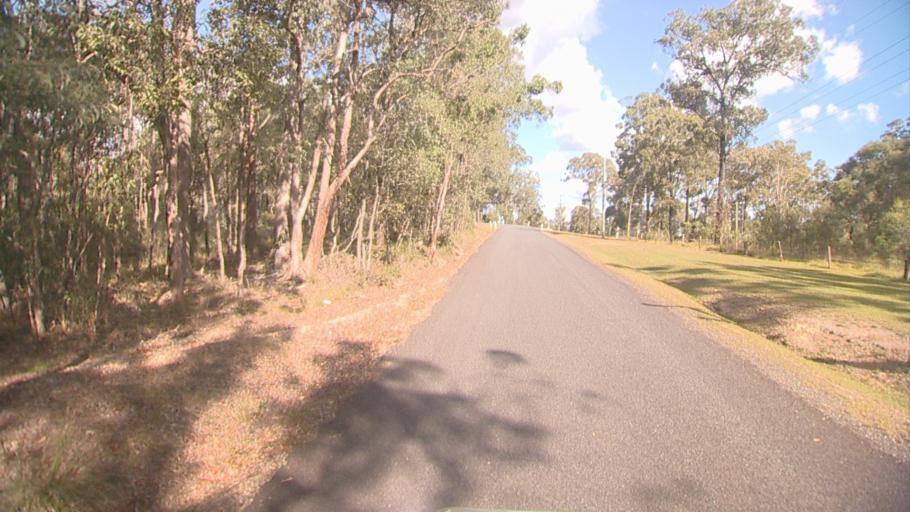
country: AU
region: Queensland
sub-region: Logan
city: Beenleigh
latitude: -27.6502
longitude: 153.2278
